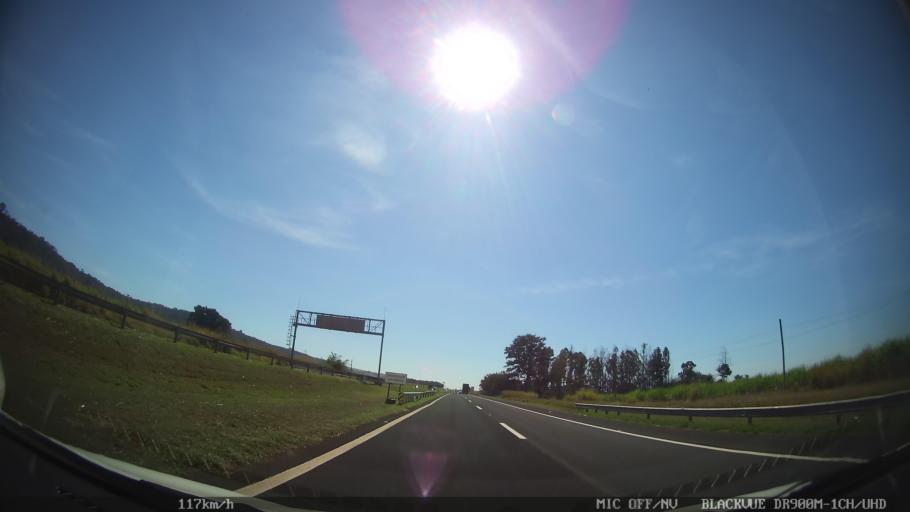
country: BR
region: Sao Paulo
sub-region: Sao Simao
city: Sao Simao
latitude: -21.5196
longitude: -47.6430
